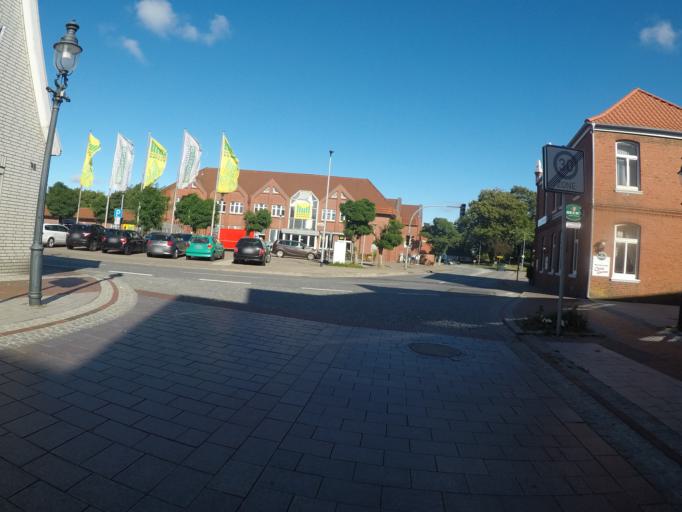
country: DE
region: Lower Saxony
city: Otterndorf
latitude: 53.8074
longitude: 8.9050
